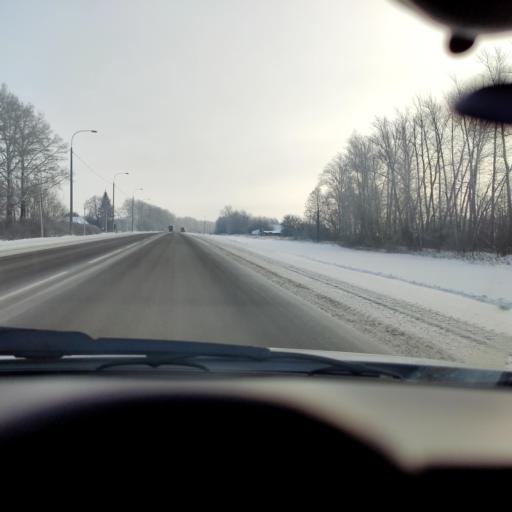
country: RU
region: Kursk
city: Kirovskiy
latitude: 51.6765
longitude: 36.5979
